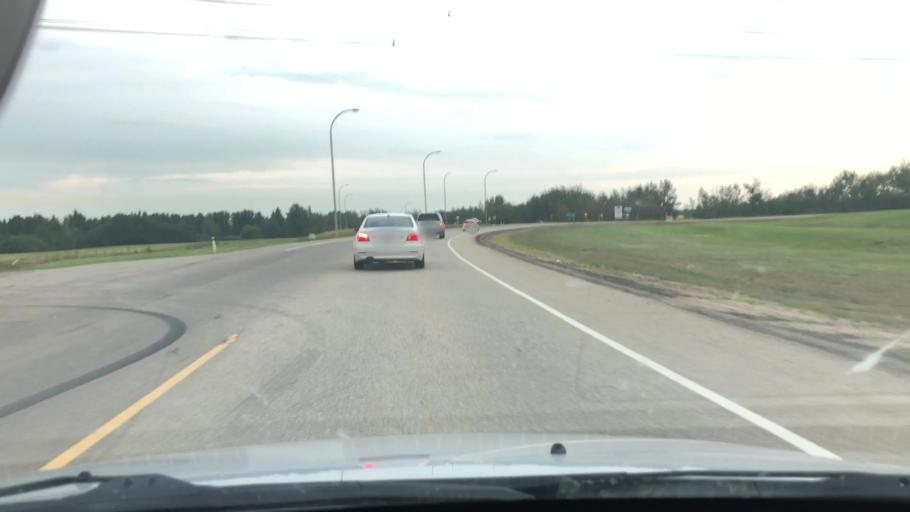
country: CA
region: Alberta
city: Devon
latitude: 53.4616
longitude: -113.6373
